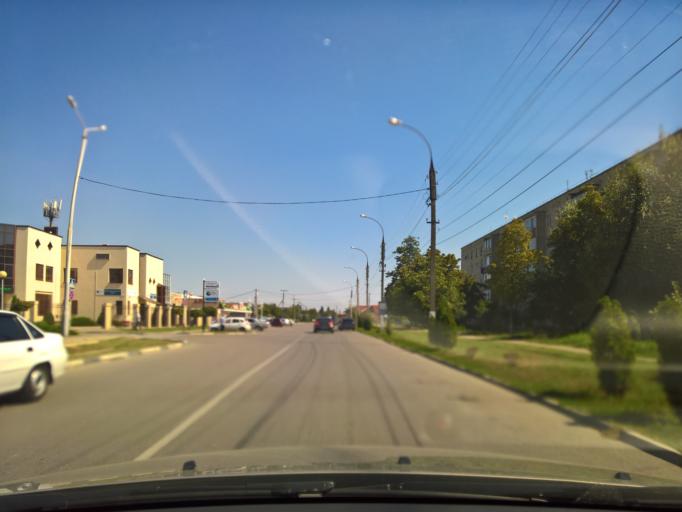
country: RU
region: Krasnodarskiy
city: Slavyansk-na-Kubani
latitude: 45.2663
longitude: 38.1070
